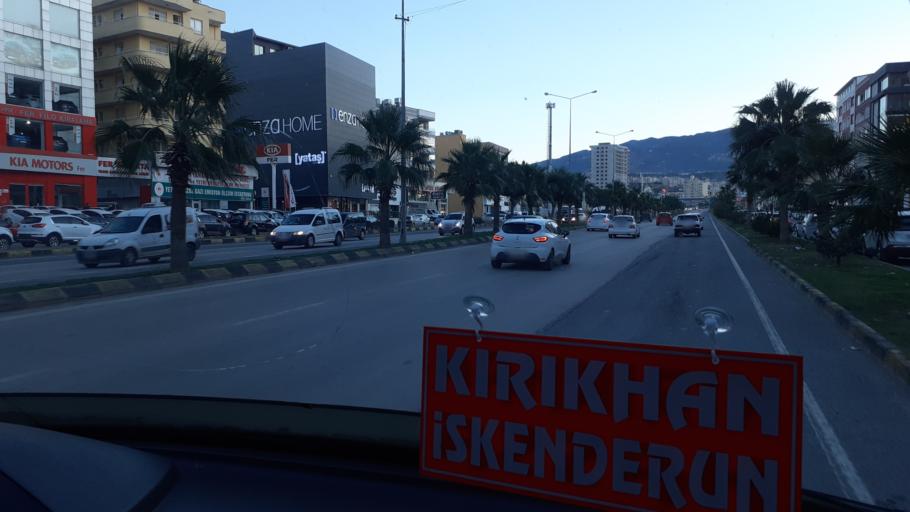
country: TR
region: Hatay
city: Iskenderun
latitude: 36.5651
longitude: 36.1569
